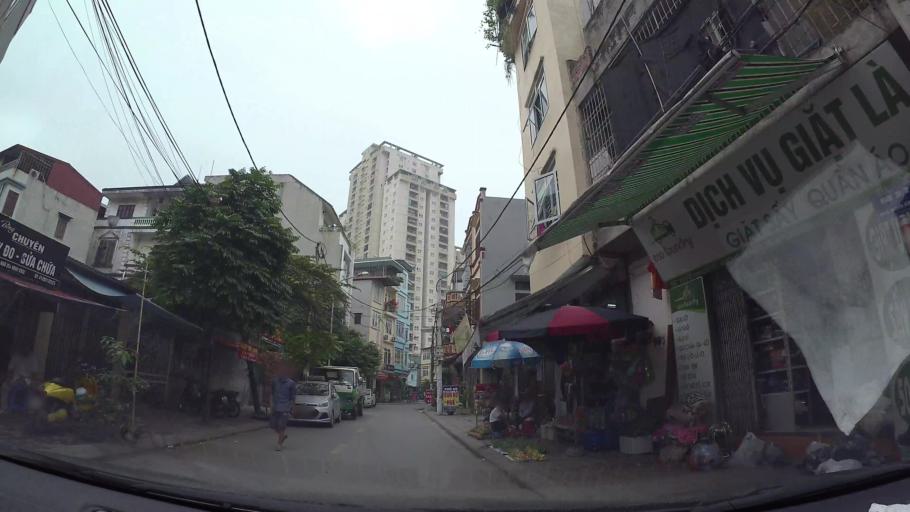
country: VN
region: Ha Noi
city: Hai BaTrung
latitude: 20.9929
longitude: 105.8586
